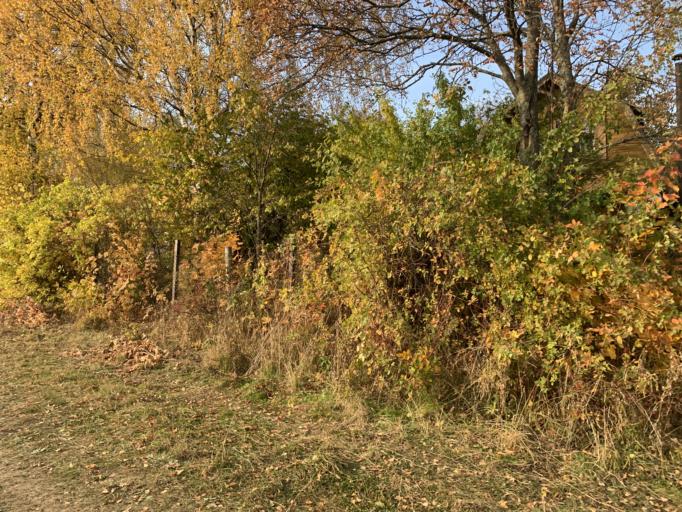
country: RU
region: Jaroslavl
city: Petrovsk
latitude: 56.9785
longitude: 39.3842
